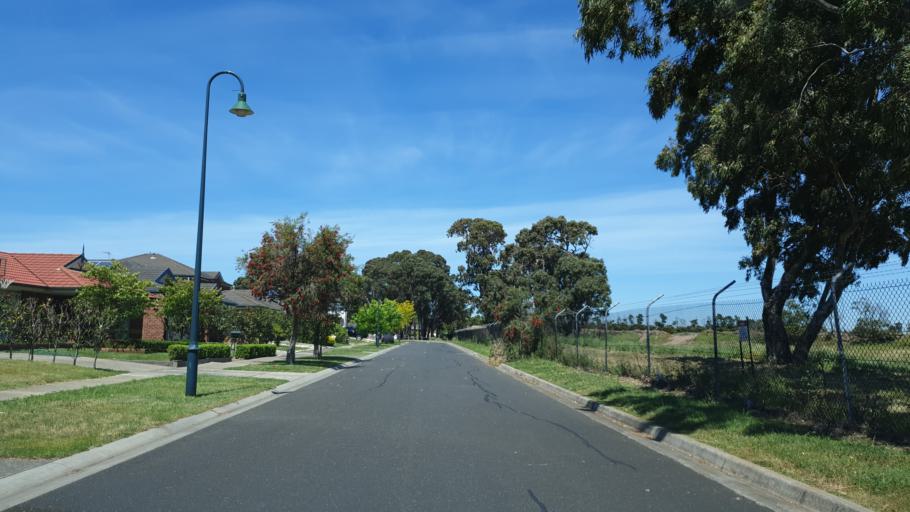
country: AU
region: Victoria
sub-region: Casey
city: Cranbourne North
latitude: -38.0640
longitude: 145.2806
